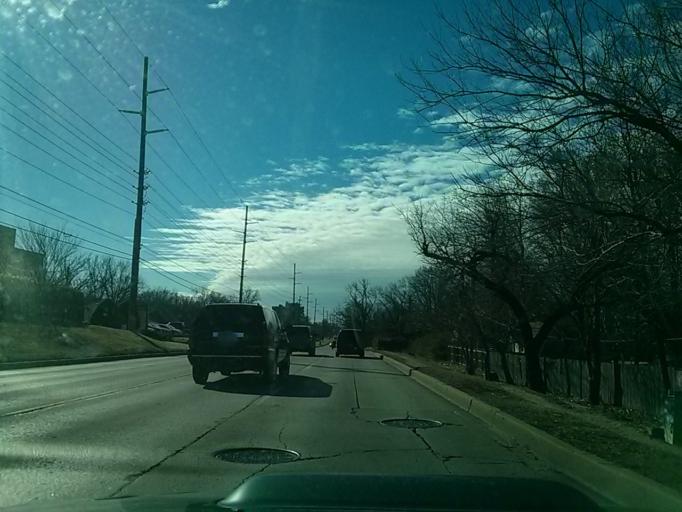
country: US
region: Oklahoma
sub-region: Tulsa County
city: Jenks
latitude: 36.0865
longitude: -95.9580
